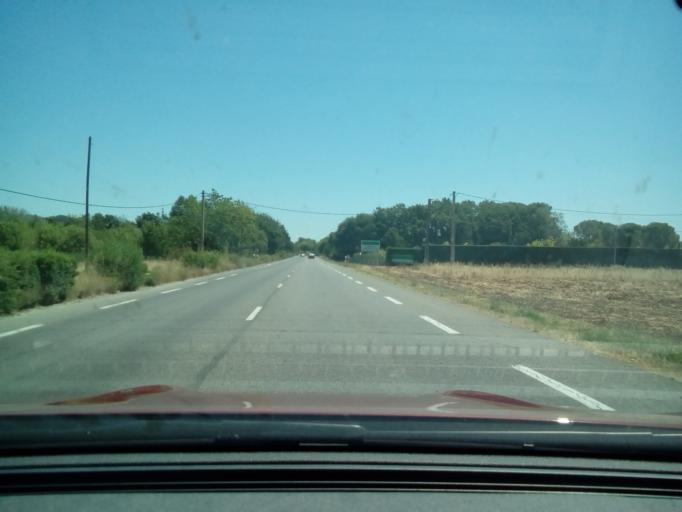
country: FR
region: Provence-Alpes-Cote d'Azur
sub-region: Departement des Bouches-du-Rhone
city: Chateauneuf-le-Rouge
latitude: 43.4797
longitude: 5.5542
